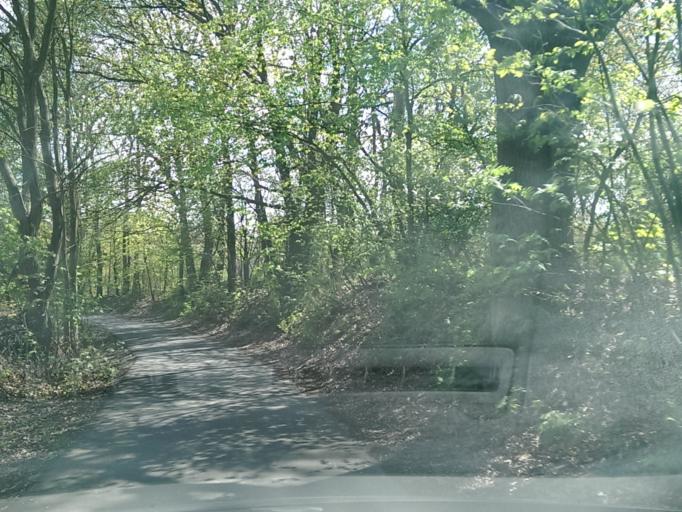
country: CZ
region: Liberecky
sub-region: Okres Semily
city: Turnov
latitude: 50.5521
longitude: 15.1396
